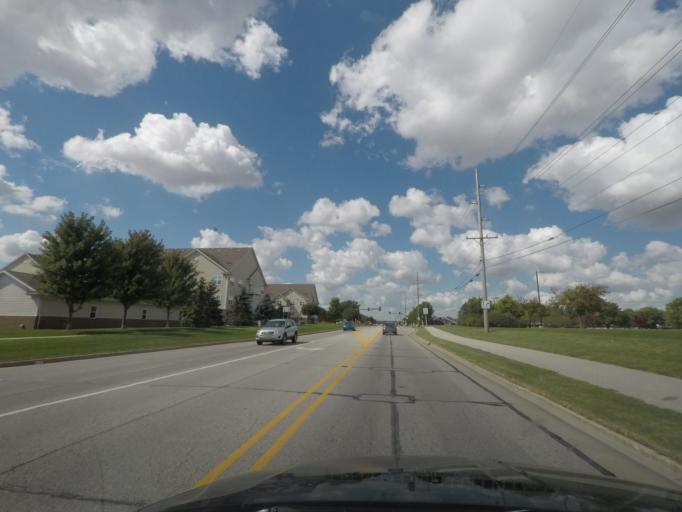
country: US
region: Iowa
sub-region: Story County
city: Ames
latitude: 42.0121
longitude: -93.6719
